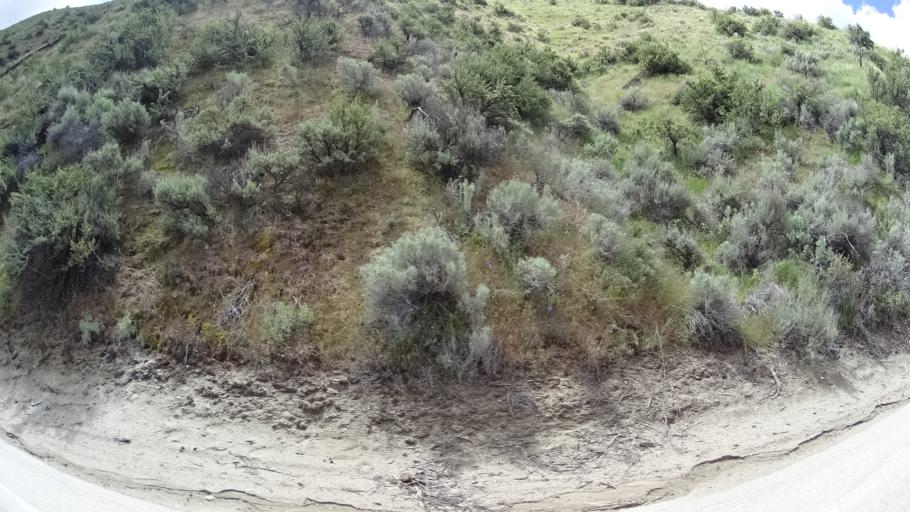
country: US
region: Idaho
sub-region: Ada County
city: Boise
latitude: 43.6869
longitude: -116.1811
